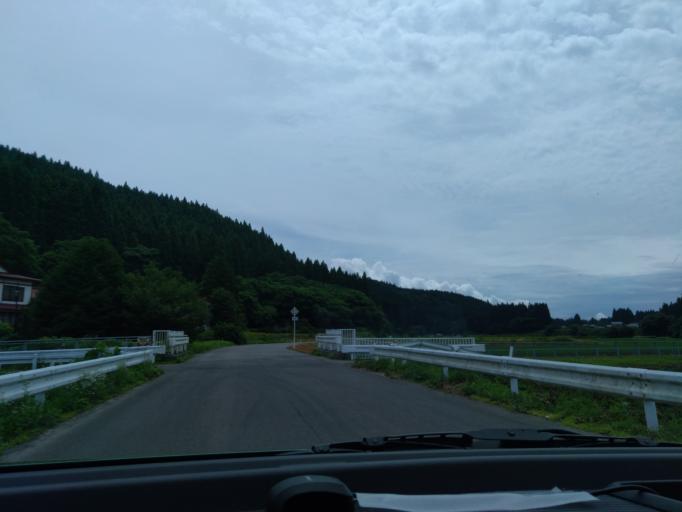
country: JP
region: Akita
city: Kakunodatemachi
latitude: 39.5941
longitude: 140.6185
